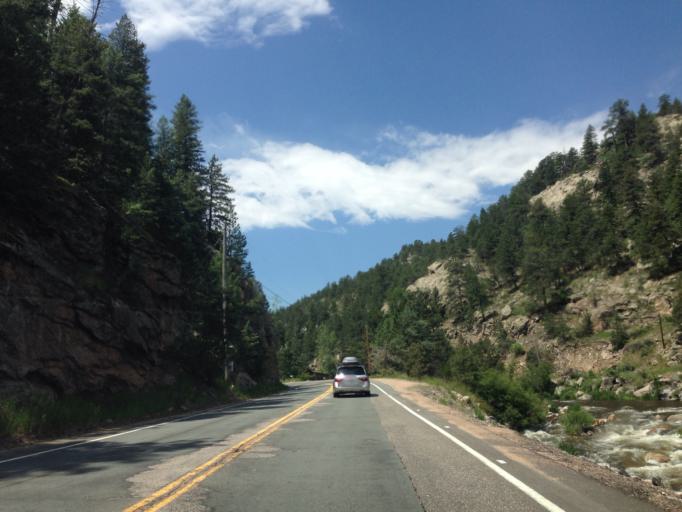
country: US
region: Colorado
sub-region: Larimer County
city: Estes Park
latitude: 40.4055
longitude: -105.4139
